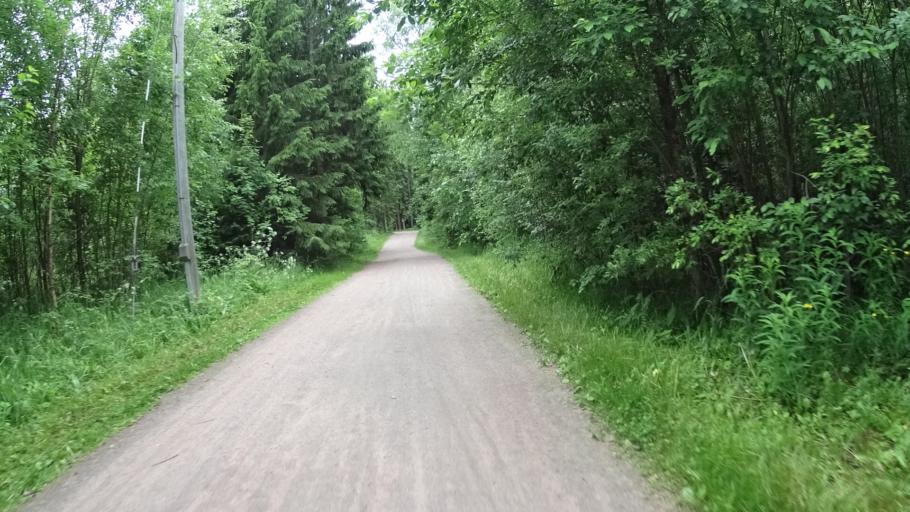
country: FI
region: Uusimaa
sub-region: Helsinki
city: Helsinki
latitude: 60.2559
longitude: 24.9075
